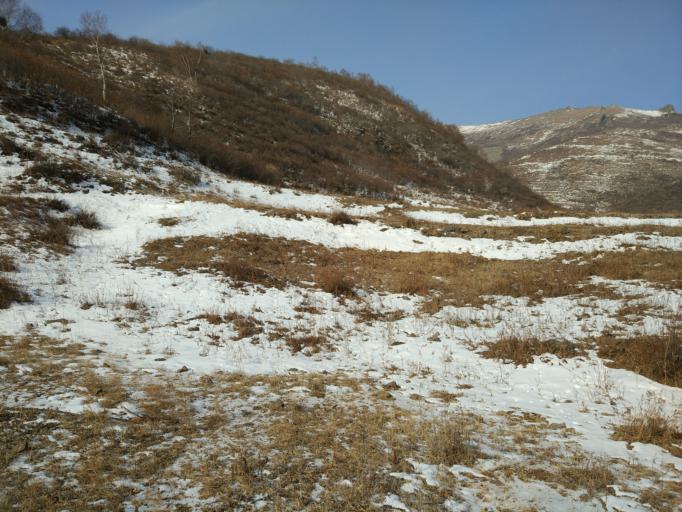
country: CN
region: Hebei
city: Xiwanzi
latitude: 40.8586
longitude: 115.4554
